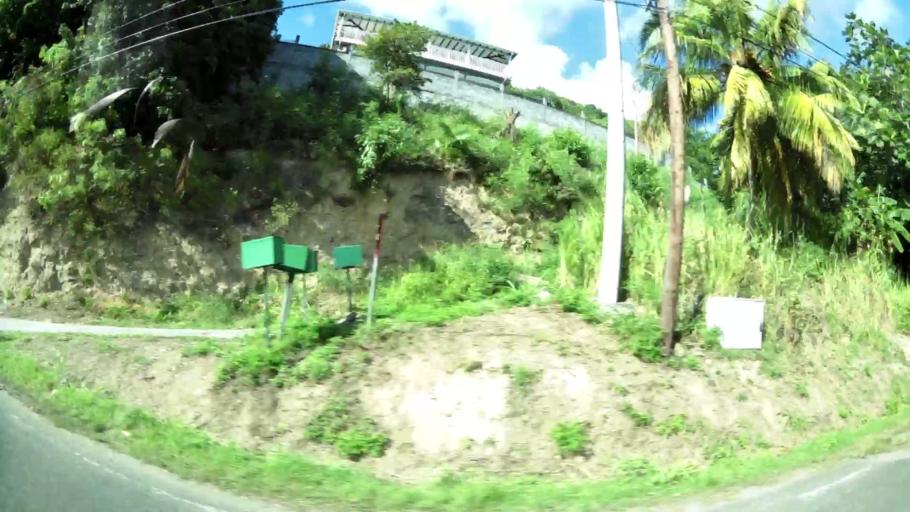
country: GP
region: Guadeloupe
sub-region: Guadeloupe
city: Le Gosier
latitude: 16.2180
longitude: -61.4878
